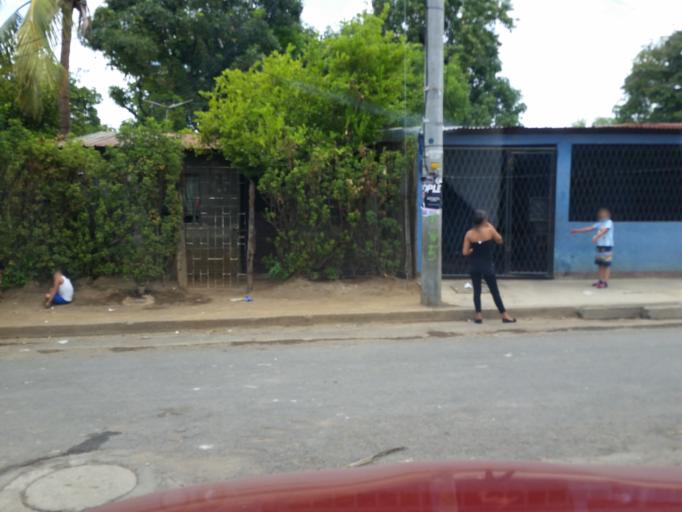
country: NI
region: Managua
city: Managua
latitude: 12.1075
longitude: -86.2479
